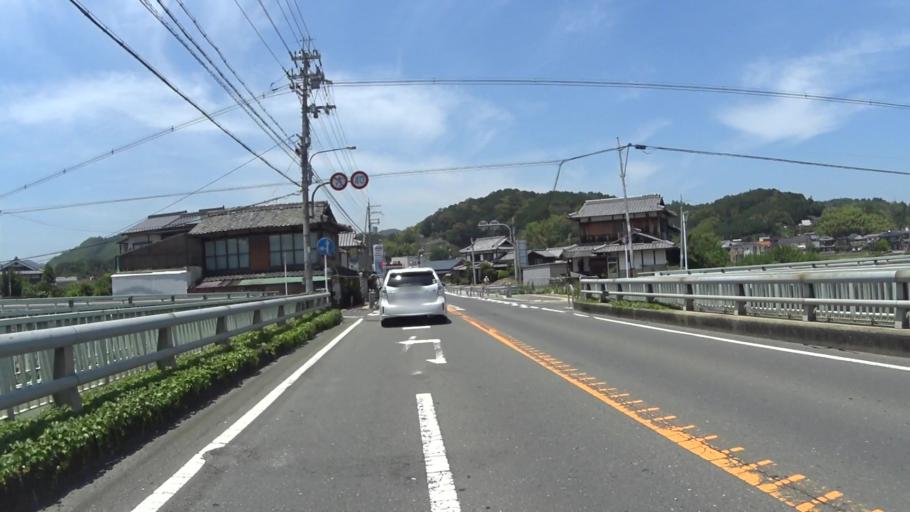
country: JP
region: Kyoto
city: Kameoka
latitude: 35.1109
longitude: 135.4701
